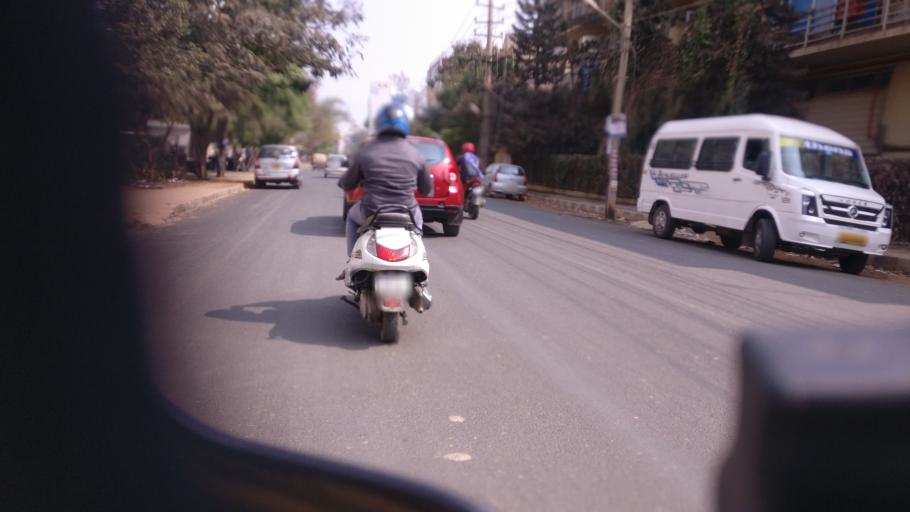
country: IN
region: Karnataka
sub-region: Bangalore Urban
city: Bangalore
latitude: 12.9008
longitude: 77.6756
